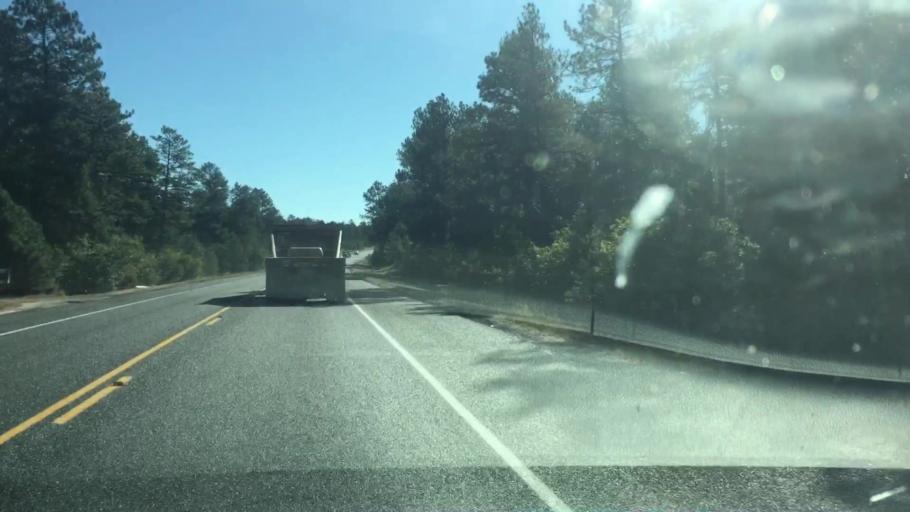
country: US
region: Colorado
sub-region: Elbert County
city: Ponderosa Park
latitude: 39.3783
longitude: -104.7027
